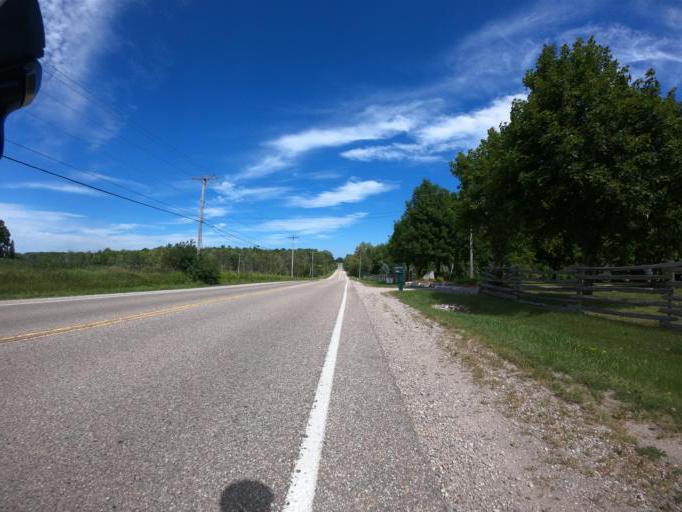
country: CA
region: Ontario
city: Waterloo
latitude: 43.5211
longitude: -80.3985
